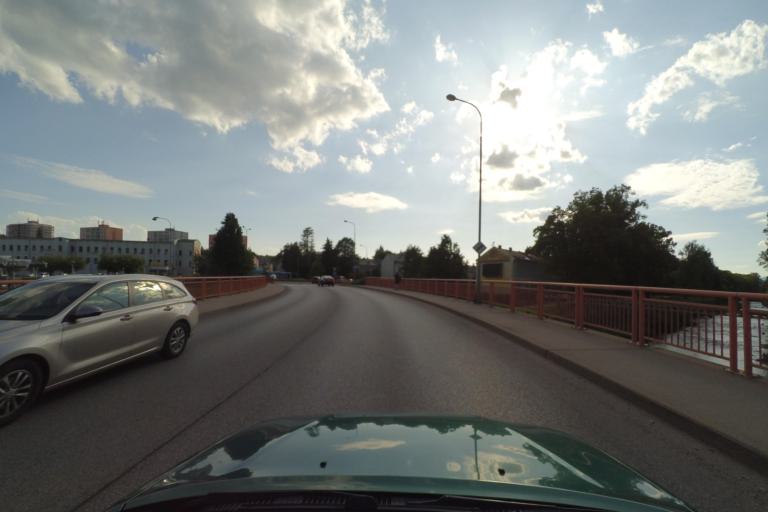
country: CZ
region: Kralovehradecky
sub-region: Okres Trutnov
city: Trutnov
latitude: 50.5655
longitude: 15.9083
